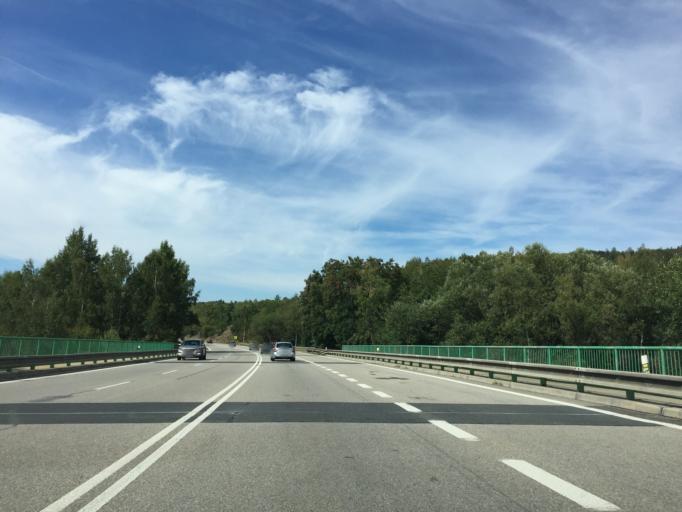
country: CZ
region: Central Bohemia
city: Votice
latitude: 49.6370
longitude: 14.6514
